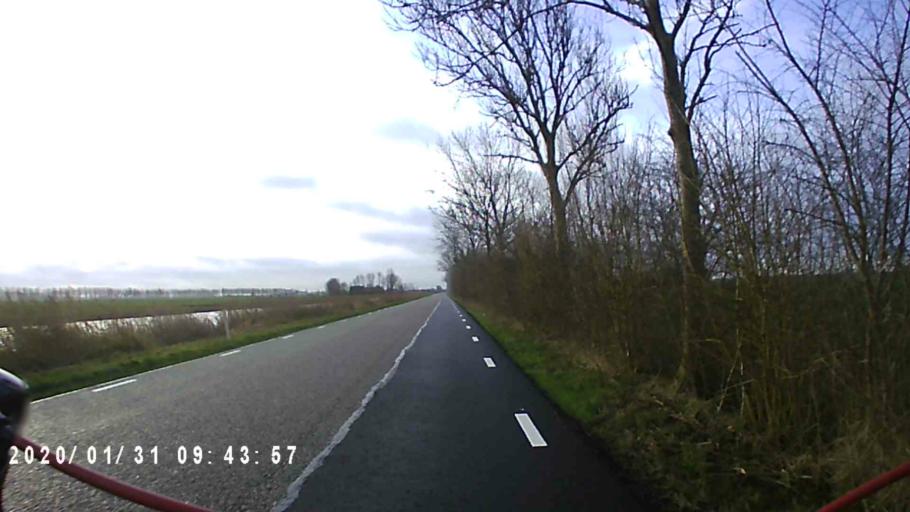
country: NL
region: Groningen
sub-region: Gemeente Zuidhorn
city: Aduard
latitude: 53.2740
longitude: 6.4842
